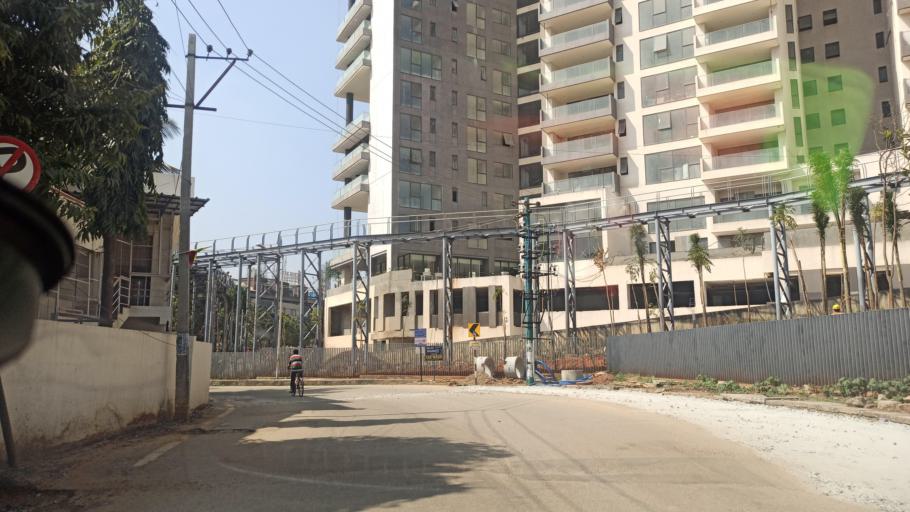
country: IN
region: Karnataka
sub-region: Bangalore Urban
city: Yelahanka
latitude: 13.0495
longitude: 77.5962
